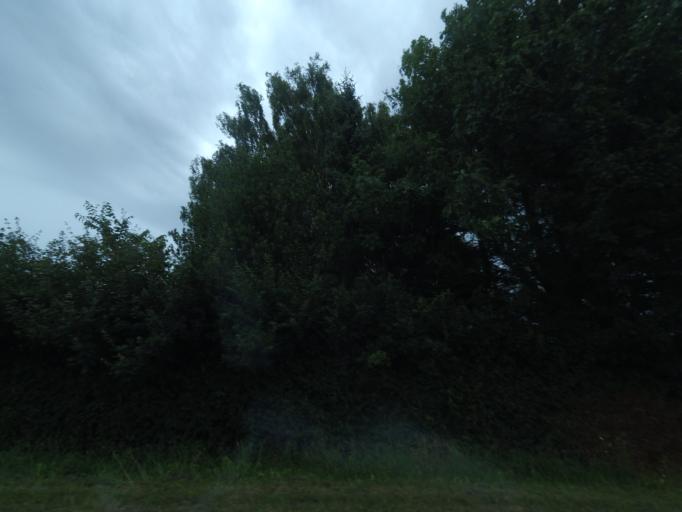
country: DK
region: South Denmark
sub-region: Middelfart Kommune
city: Norre Aby
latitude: 55.4663
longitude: 9.9094
